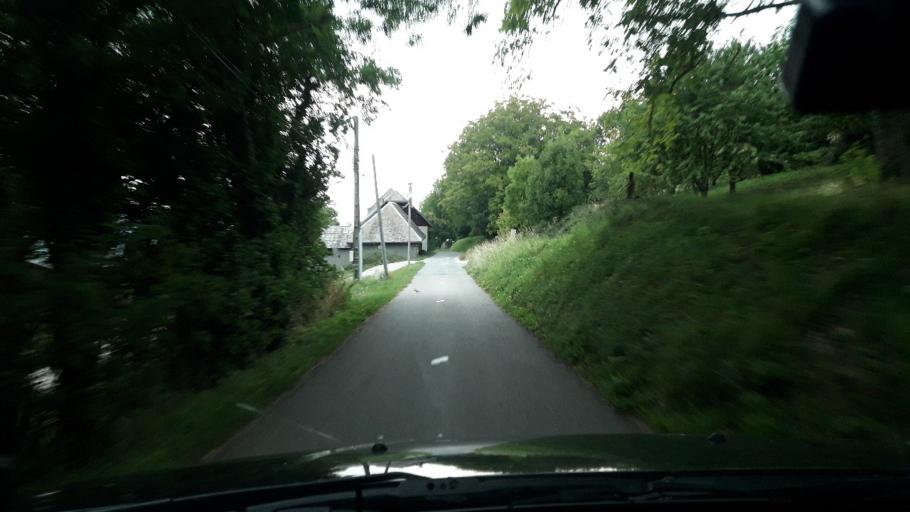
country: FR
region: Rhone-Alpes
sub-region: Departement de la Savoie
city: Barberaz
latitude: 45.5232
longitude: 5.9252
